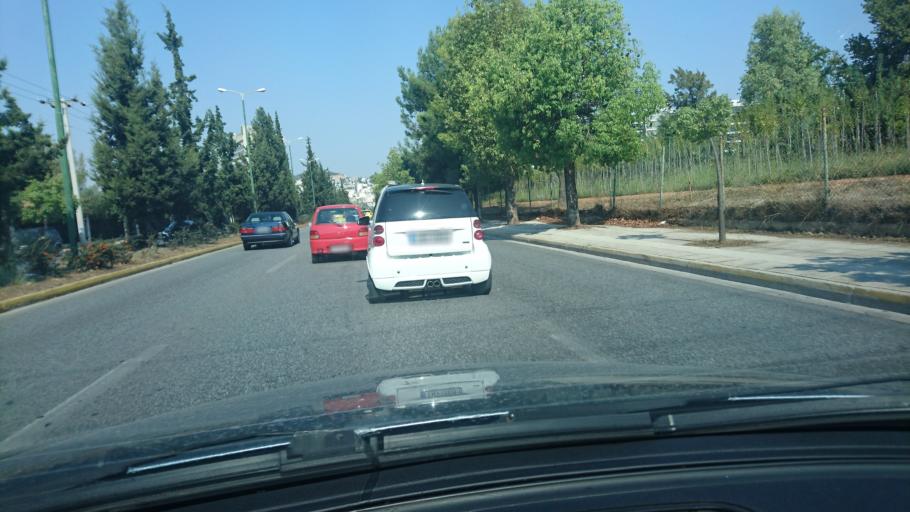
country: GR
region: Attica
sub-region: Nomarchia Athinas
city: Papagou
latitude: 37.9868
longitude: 23.7808
